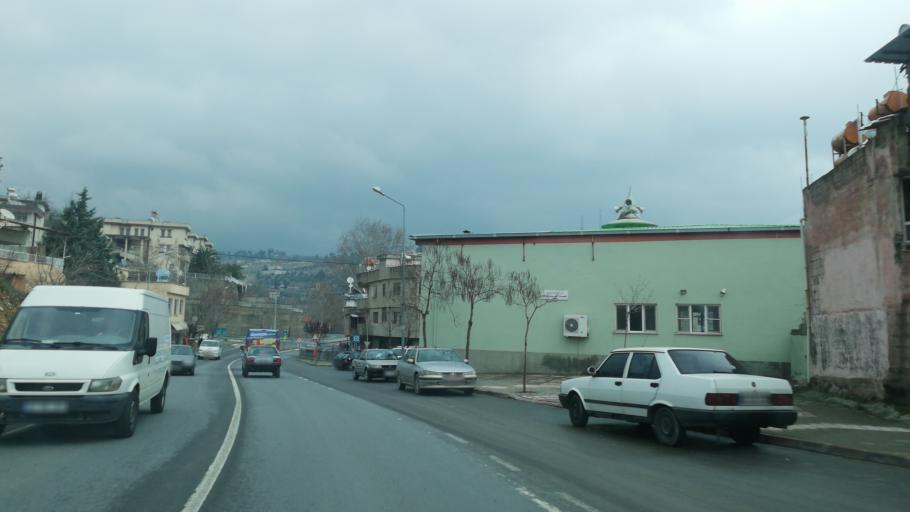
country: TR
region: Kahramanmaras
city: Kahramanmaras
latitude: 37.5927
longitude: 36.9326
